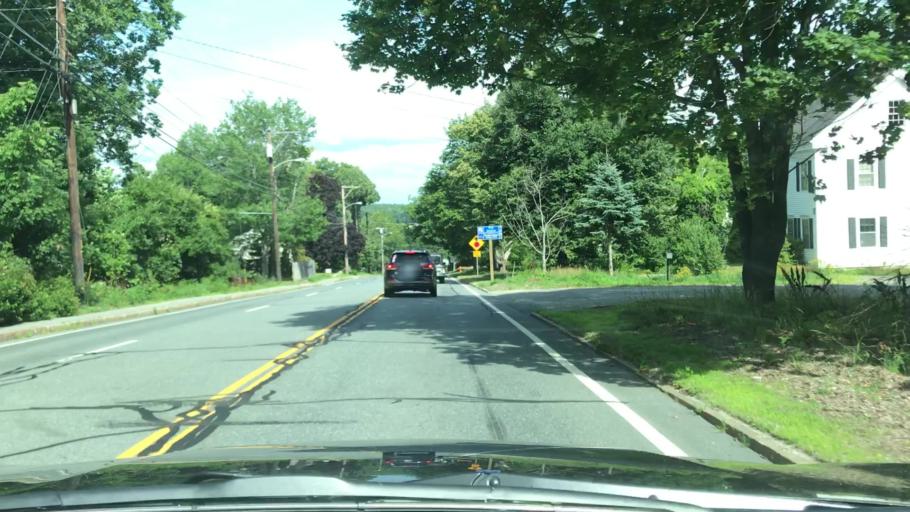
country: US
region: Maine
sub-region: Hancock County
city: Ellsworth
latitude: 44.5391
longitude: -68.4337
